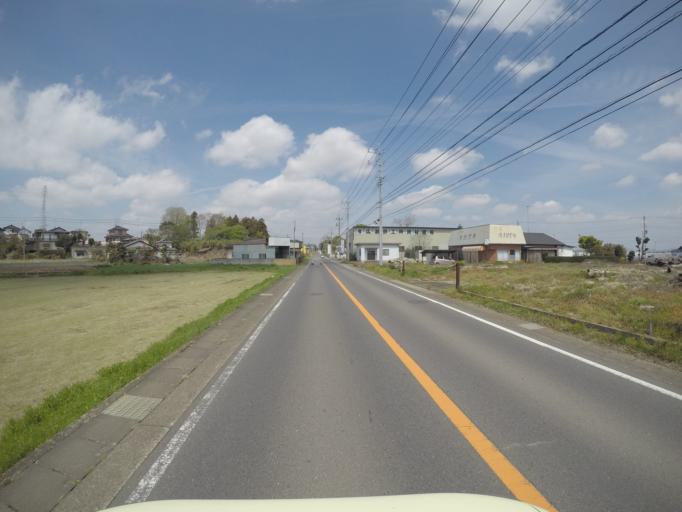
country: JP
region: Ibaraki
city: Shimodate
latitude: 36.2642
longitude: 140.0220
